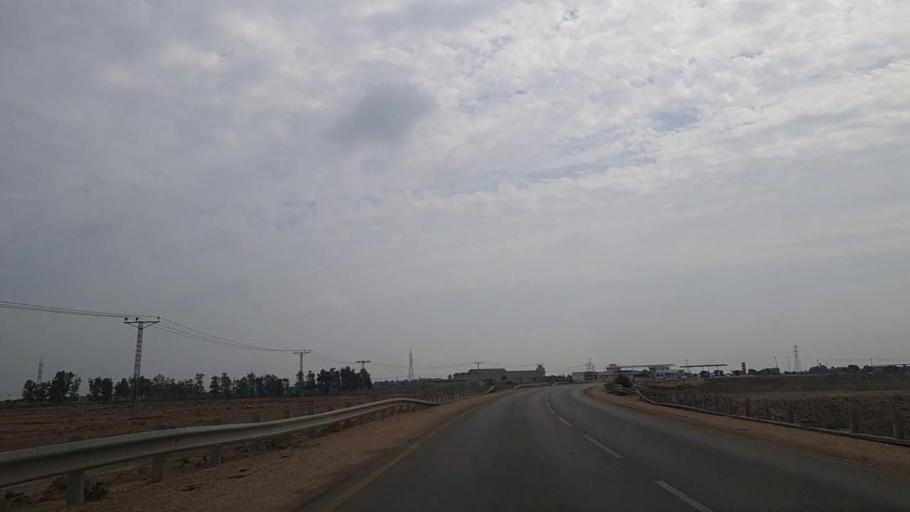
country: PK
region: Sindh
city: Daro Mehar
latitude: 24.6174
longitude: 68.0863
